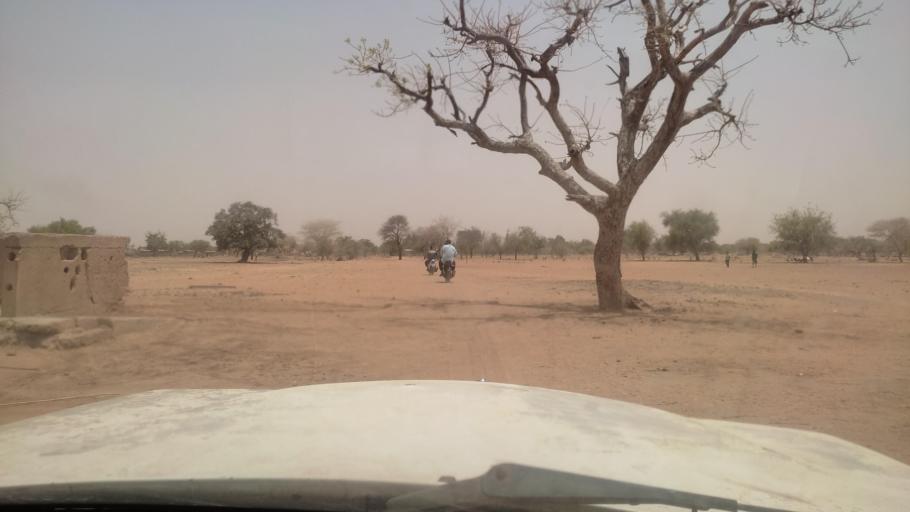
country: BF
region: Est
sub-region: Gnagna Province
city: Bogande
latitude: 13.0049
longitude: -0.0923
